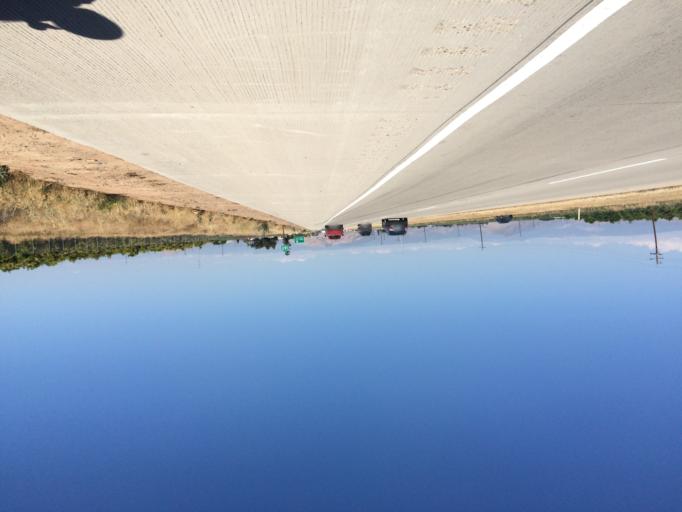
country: US
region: California
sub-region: Fresno County
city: Sanger
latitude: 36.7358
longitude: -119.6164
